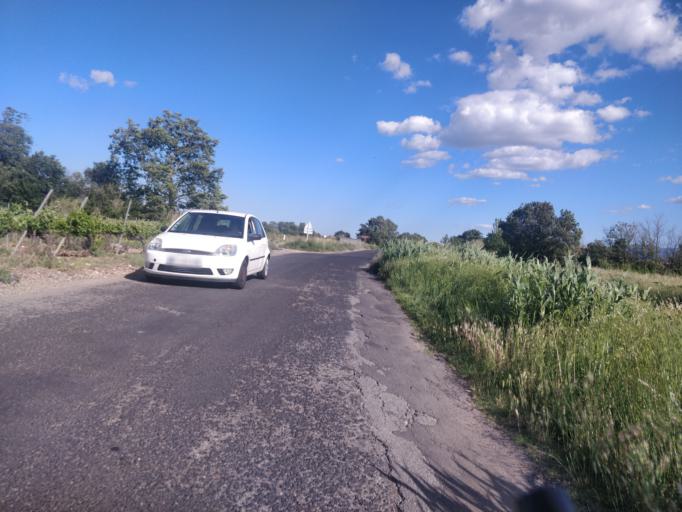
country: FR
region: Languedoc-Roussillon
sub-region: Departement des Pyrenees-Orientales
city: Cabestany
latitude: 42.6661
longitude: 2.9344
